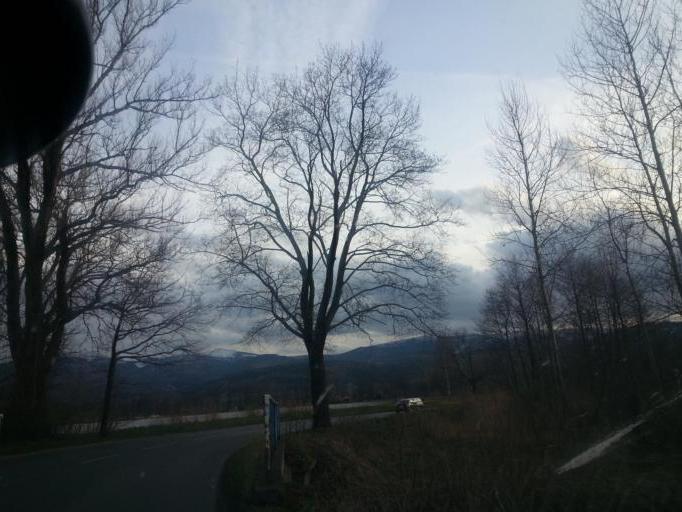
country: PL
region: Lower Silesian Voivodeship
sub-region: Jelenia Gora
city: Cieplice Slaskie Zdroj
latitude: 50.8491
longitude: 15.6867
